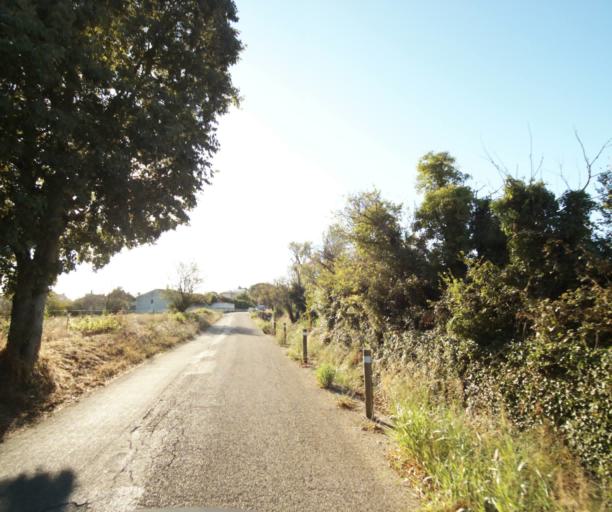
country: FR
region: Languedoc-Roussillon
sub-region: Departement du Gard
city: Bouillargues
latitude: 43.8030
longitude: 4.4198
